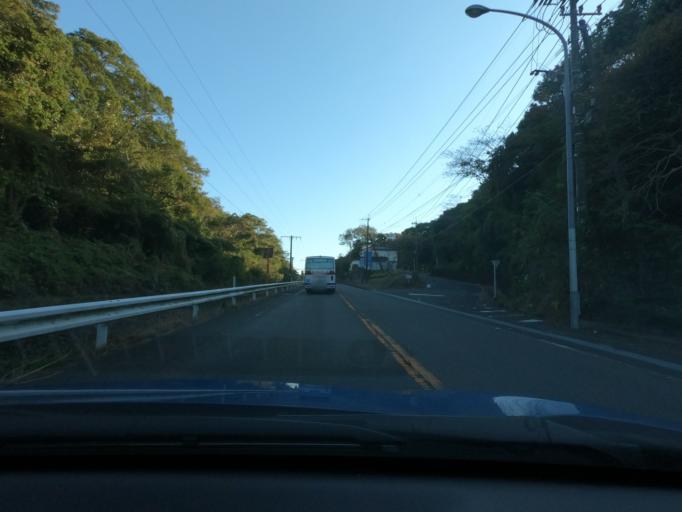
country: JP
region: Kagoshima
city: Akune
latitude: 31.9984
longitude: 130.1960
